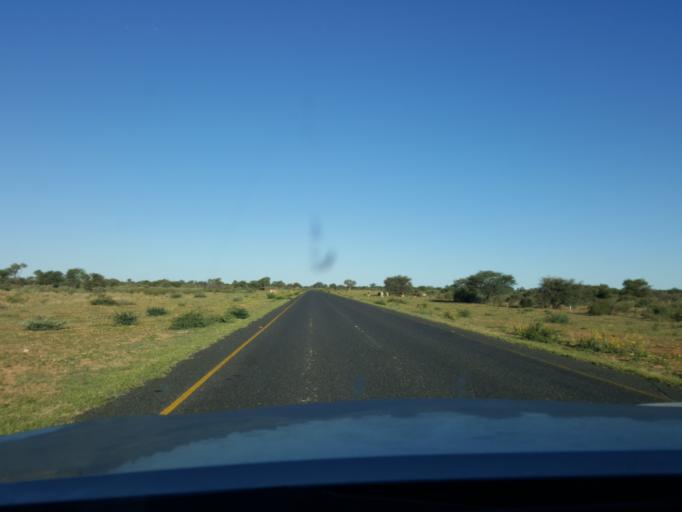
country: BW
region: Southern
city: Khakhea
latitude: -24.2490
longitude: 23.2898
